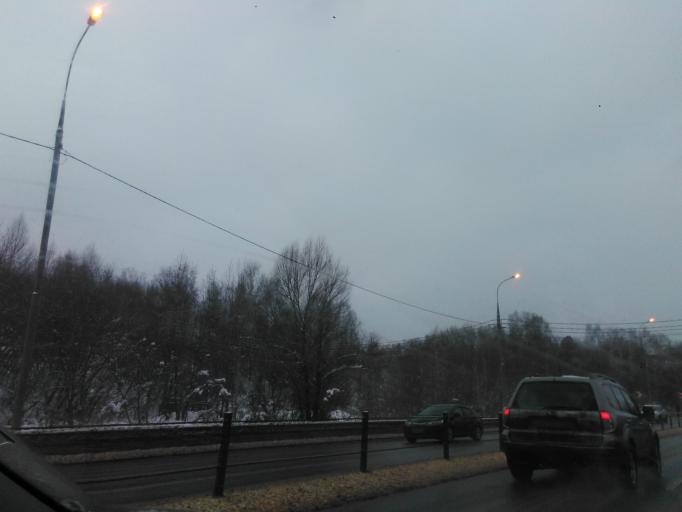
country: RU
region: Moskovskaya
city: Dedenevo
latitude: 56.2511
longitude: 37.5150
